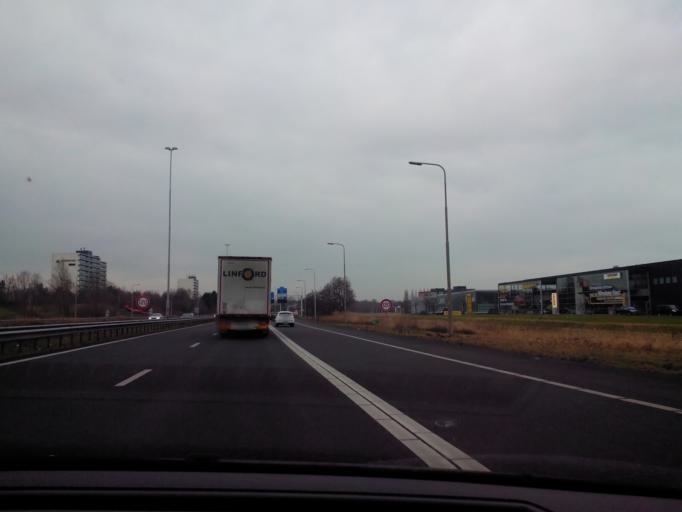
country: NL
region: North Brabant
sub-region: Gemeente Breda
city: Hoge Vucht
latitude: 51.5824
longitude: 4.8240
